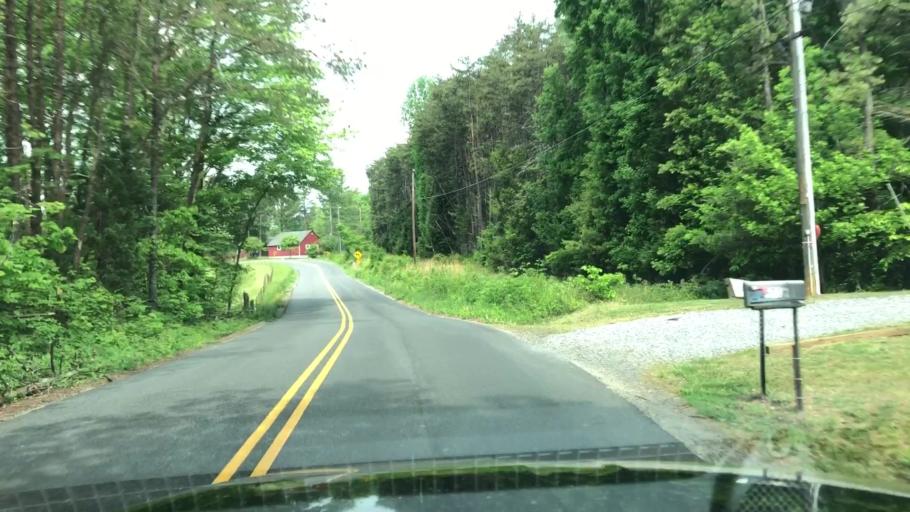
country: US
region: Virginia
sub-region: Stafford County
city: Stafford
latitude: 38.4469
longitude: -77.4928
